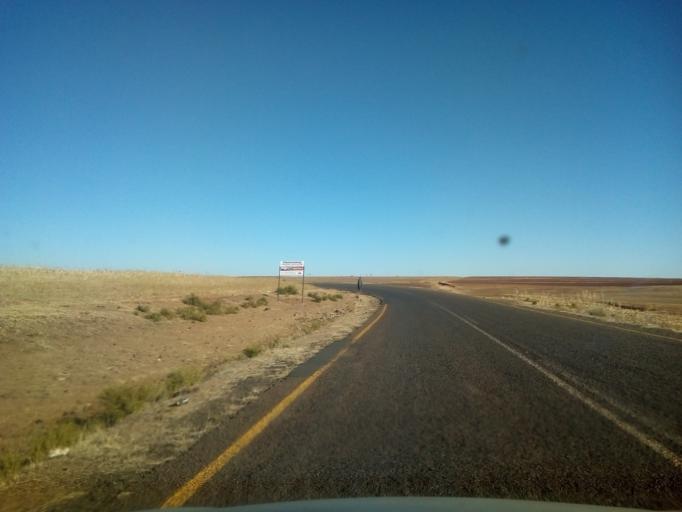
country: LS
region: Berea
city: Teyateyaneng
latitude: -29.2819
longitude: 27.6628
